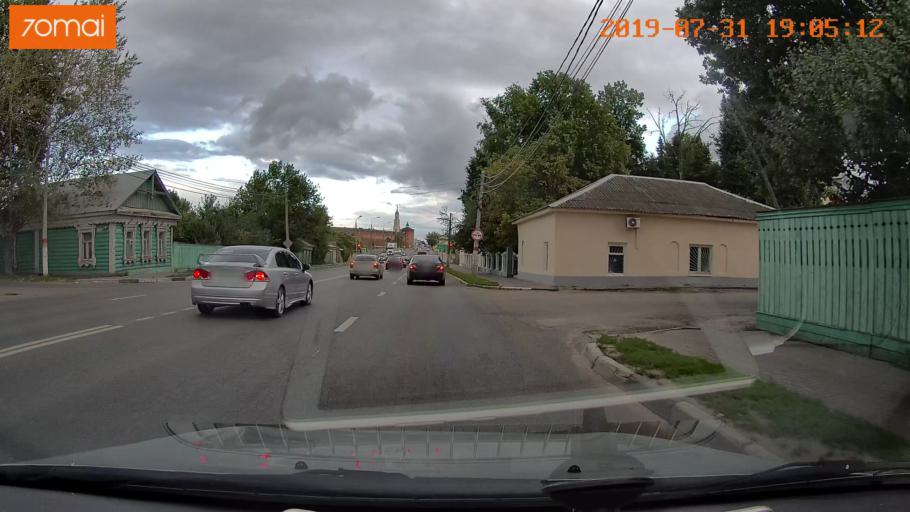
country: RU
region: Moskovskaya
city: Raduzhnyy
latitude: 55.1064
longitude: 38.7455
